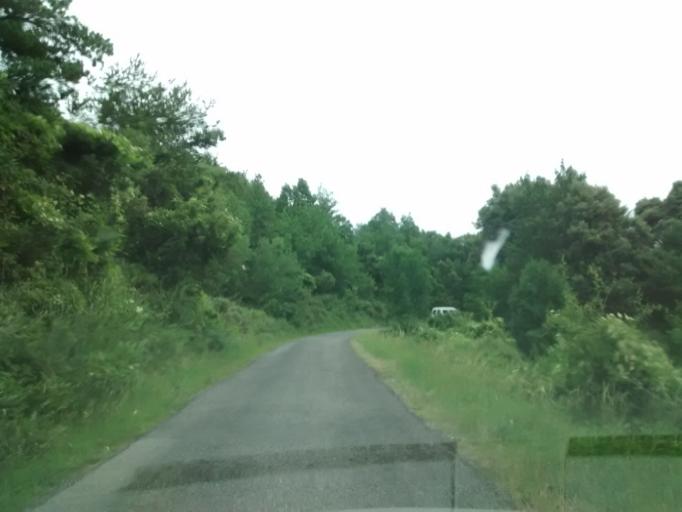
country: ES
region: Aragon
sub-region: Provincia de Huesca
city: Puertolas
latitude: 42.5419
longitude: 0.1295
